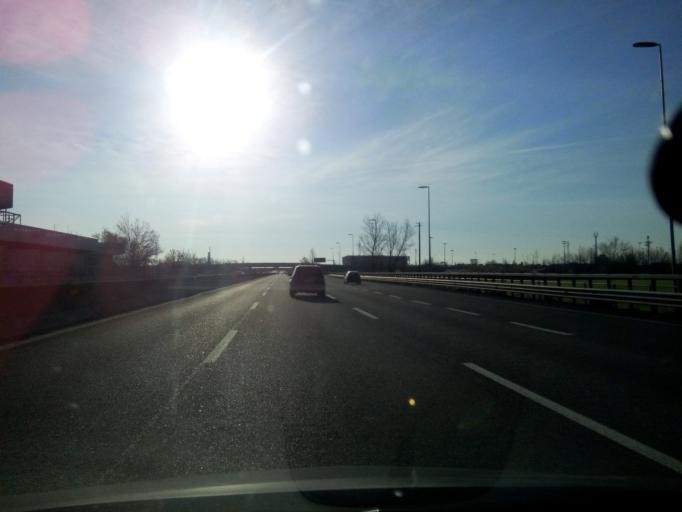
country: IT
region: Emilia-Romagna
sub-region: Provincia di Parma
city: Baganzola
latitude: 44.8416
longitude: 10.3316
